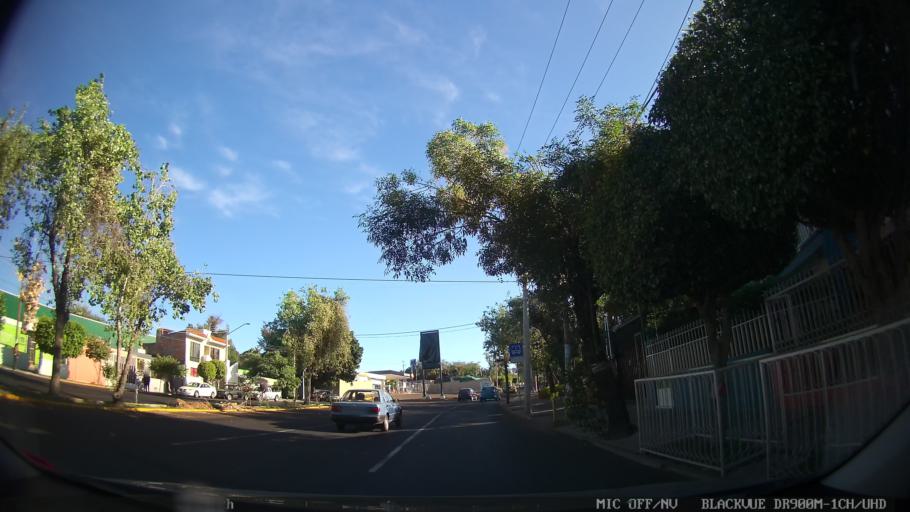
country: MX
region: Jalisco
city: Tlaquepaque
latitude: 20.6813
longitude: -103.2946
